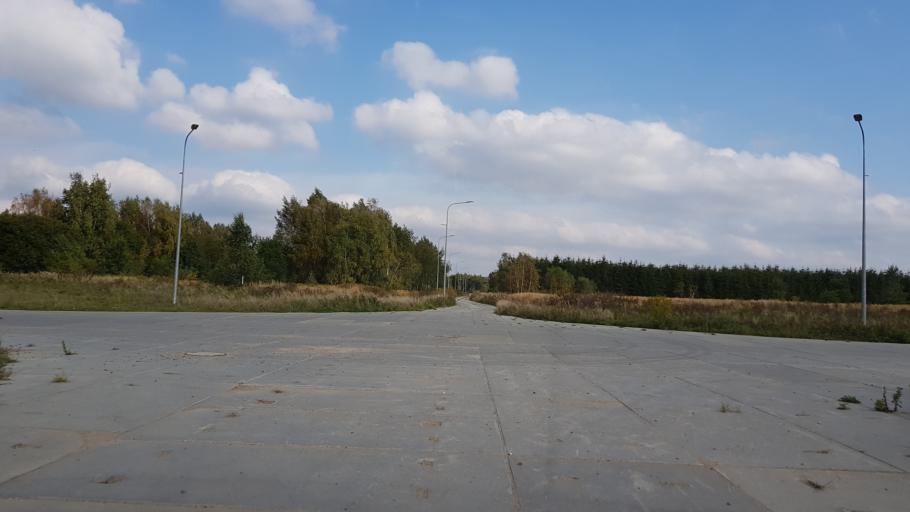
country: PL
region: West Pomeranian Voivodeship
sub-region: Koszalin
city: Koszalin
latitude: 54.1771
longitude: 16.1561
